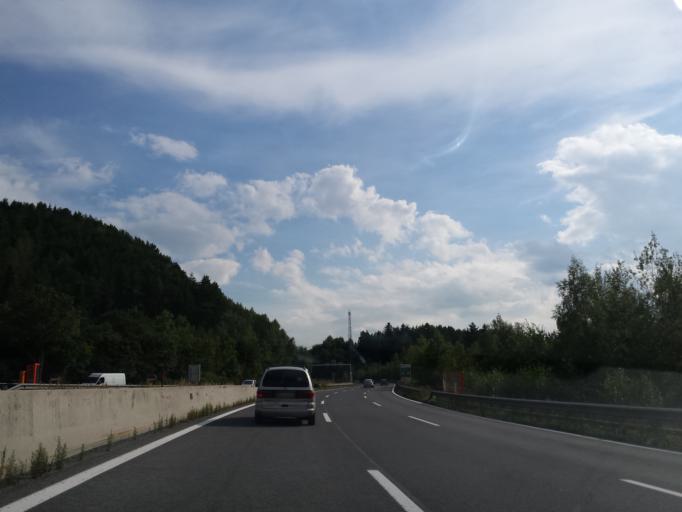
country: AT
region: Lower Austria
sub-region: Politischer Bezirk Neunkirchen
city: Edlitz
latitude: 47.5762
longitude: 16.1130
